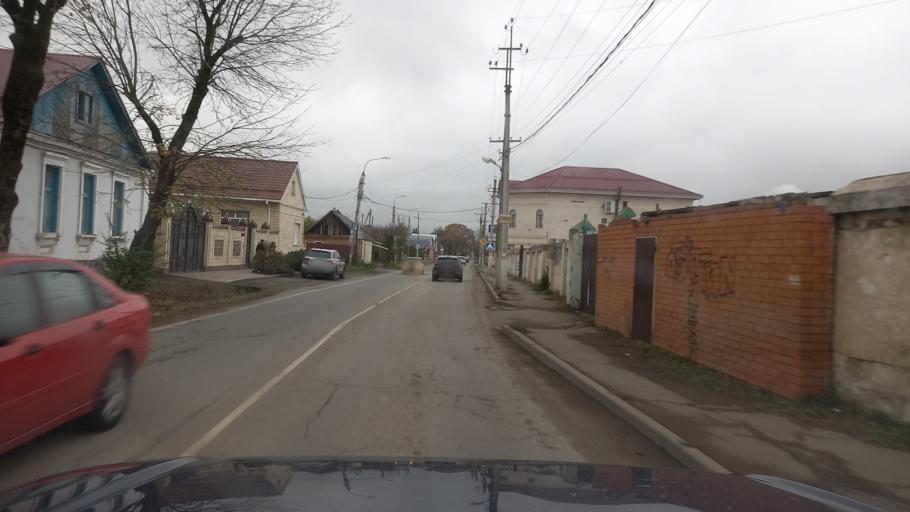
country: RU
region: Adygeya
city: Maykop
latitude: 44.6067
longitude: 40.0925
